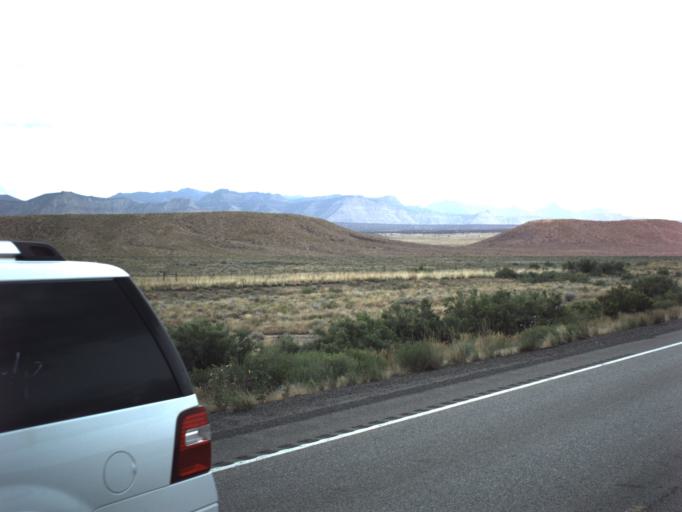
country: US
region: Utah
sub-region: Carbon County
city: East Carbon City
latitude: 39.4609
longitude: -110.4872
